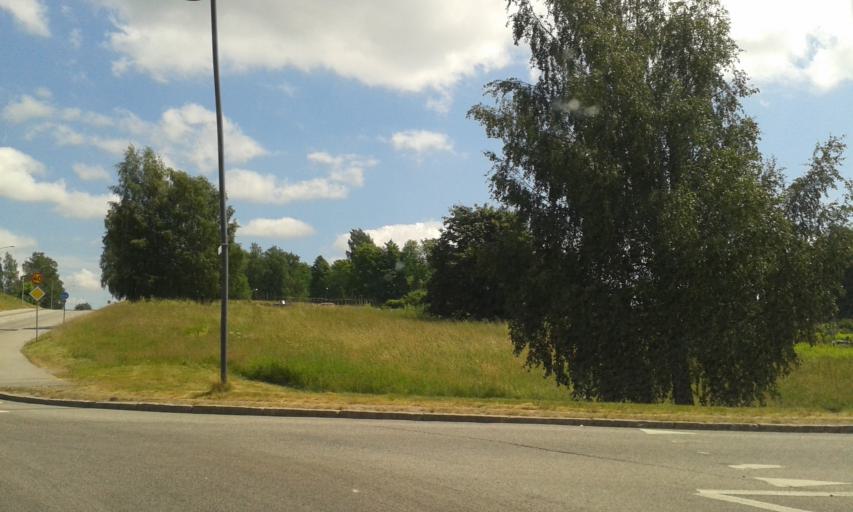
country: SE
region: Kronoberg
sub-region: Vaxjo Kommun
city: Vaexjoe
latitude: 56.8810
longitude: 14.8153
